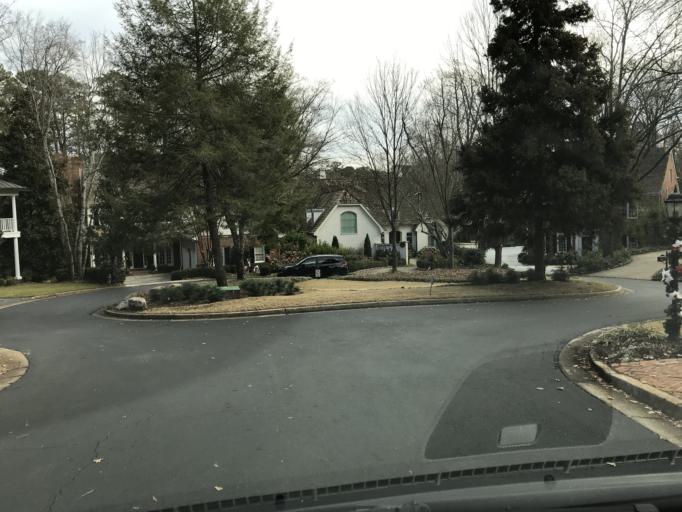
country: US
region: Georgia
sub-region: DeKalb County
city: North Atlanta
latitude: 33.8715
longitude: -84.3448
